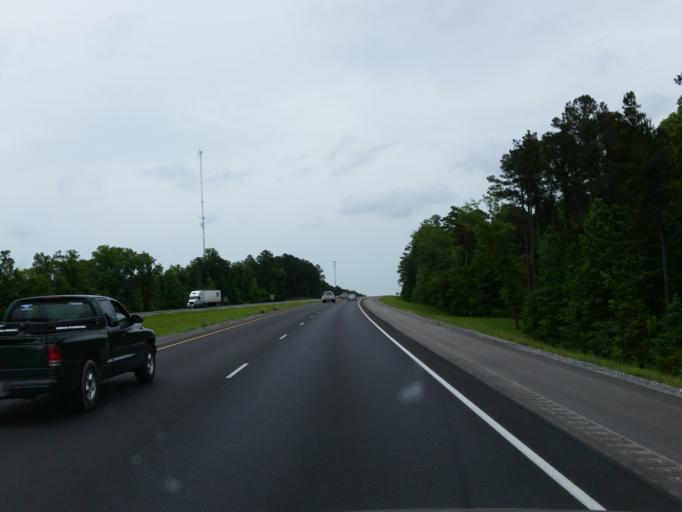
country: US
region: Mississippi
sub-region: Jones County
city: Sharon
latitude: 31.9591
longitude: -88.9732
